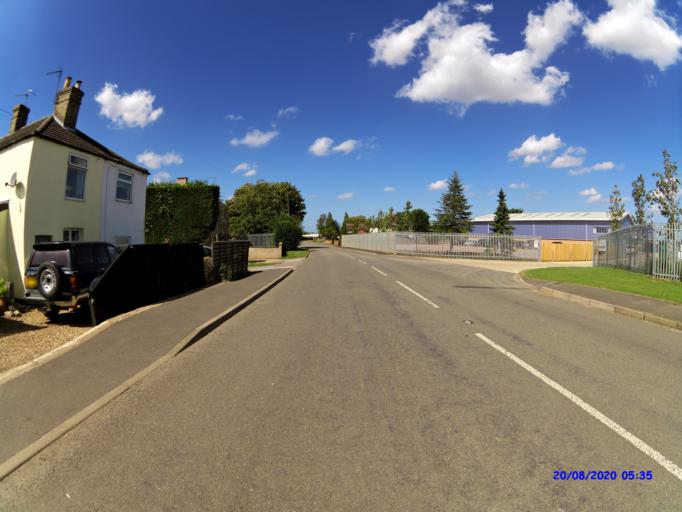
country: GB
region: England
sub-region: Cambridgeshire
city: Whittlesey
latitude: 52.5456
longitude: -0.1138
